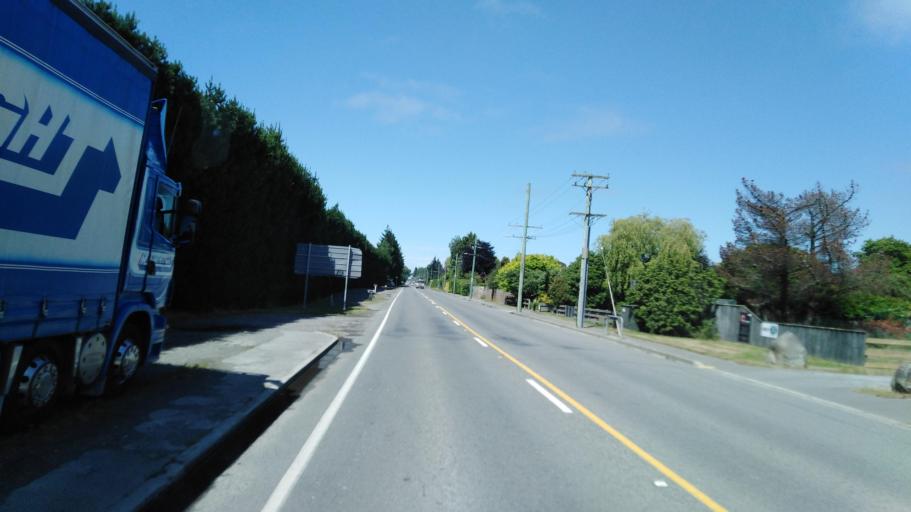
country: NZ
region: Canterbury
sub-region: Selwyn District
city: Prebbleton
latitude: -43.5134
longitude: 172.5084
